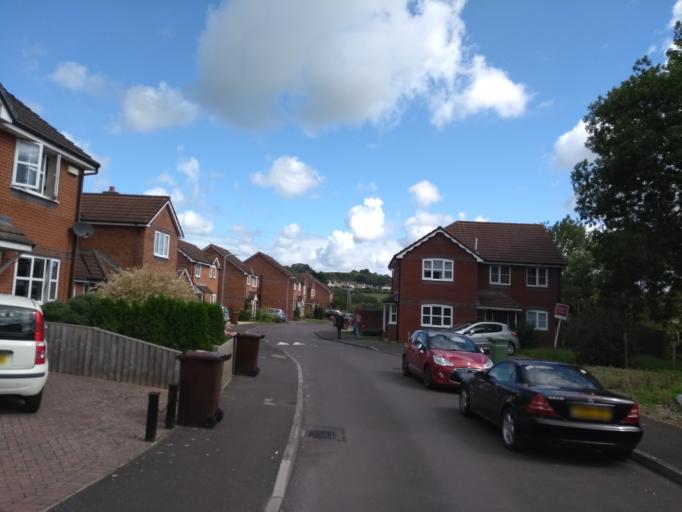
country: GB
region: England
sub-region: Somerset
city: Street
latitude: 51.1321
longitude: -2.7318
